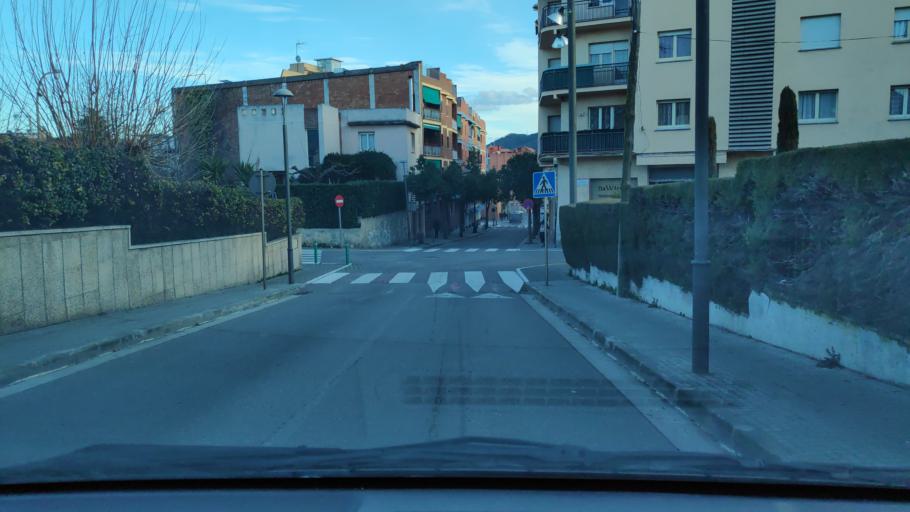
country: ES
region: Catalonia
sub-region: Provincia de Barcelona
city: Montmelo
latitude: 41.5529
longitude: 2.2466
